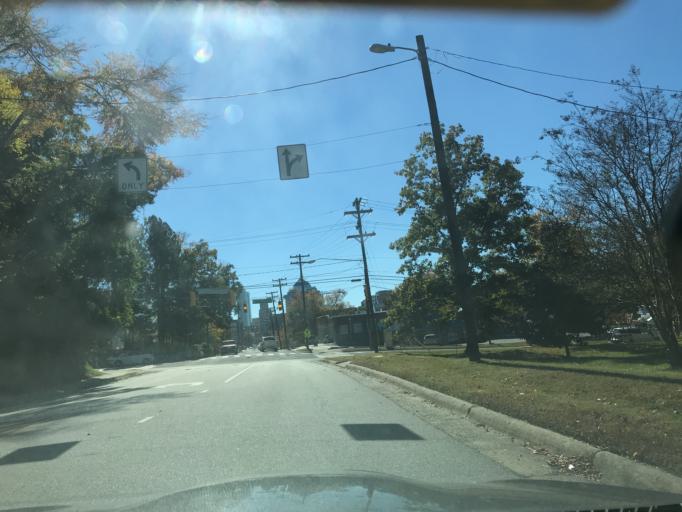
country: US
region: North Carolina
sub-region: Durham County
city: Durham
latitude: 36.0060
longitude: -78.9014
